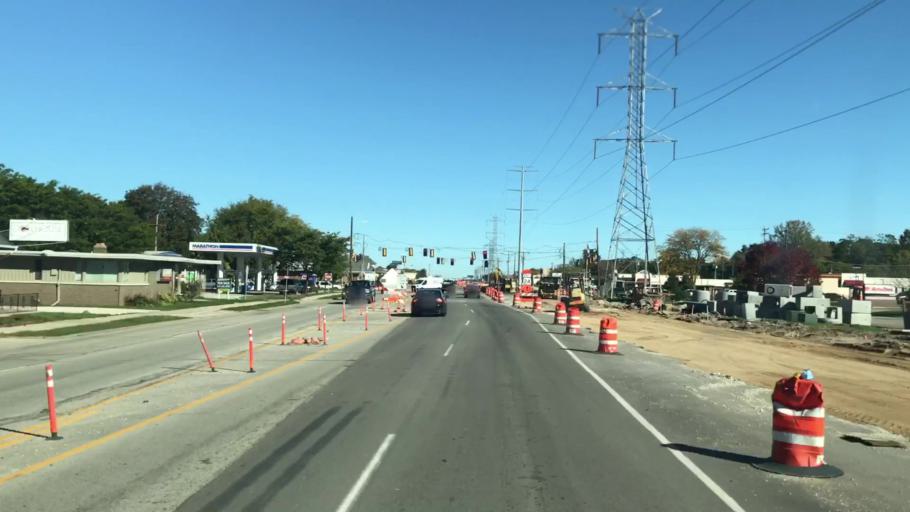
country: US
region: Wisconsin
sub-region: Milwaukee County
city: Hales Corners
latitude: 42.9433
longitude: -88.0484
